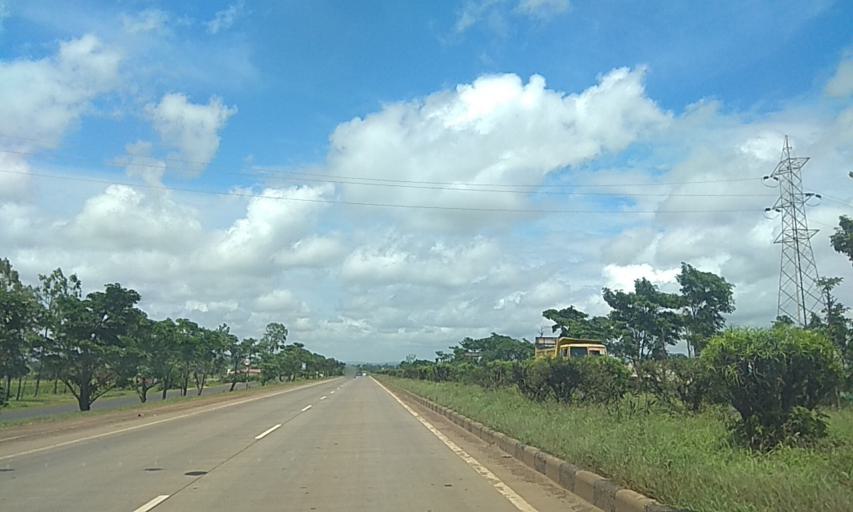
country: IN
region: Karnataka
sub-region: Belgaum
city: Sankeshwar
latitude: 16.1495
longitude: 74.5174
